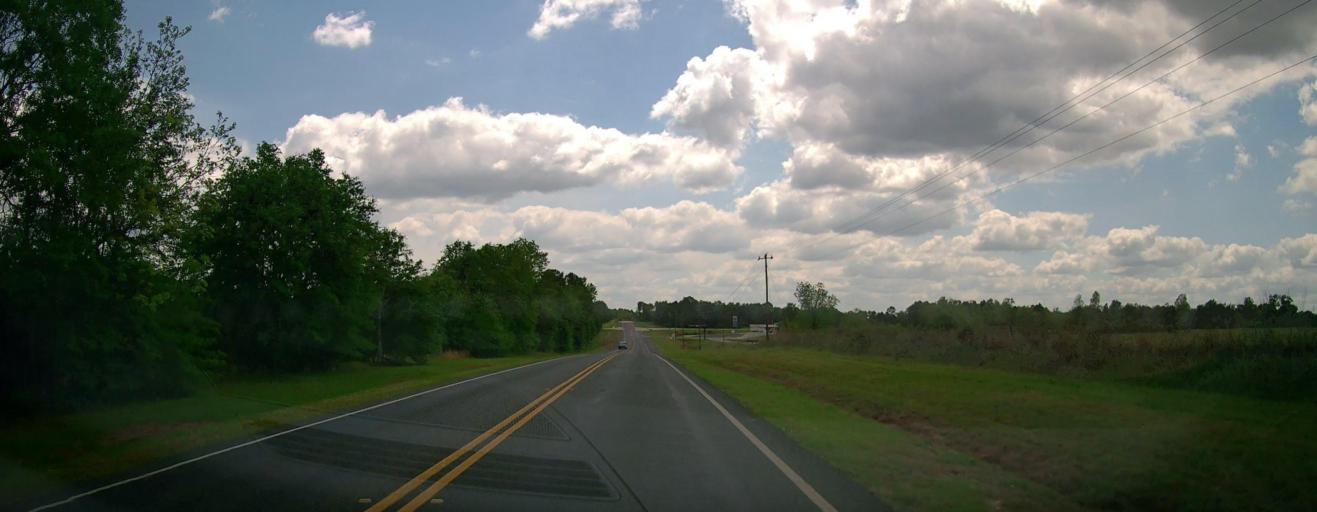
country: US
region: Georgia
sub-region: Treutlen County
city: Soperton
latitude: 32.4403
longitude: -82.6068
